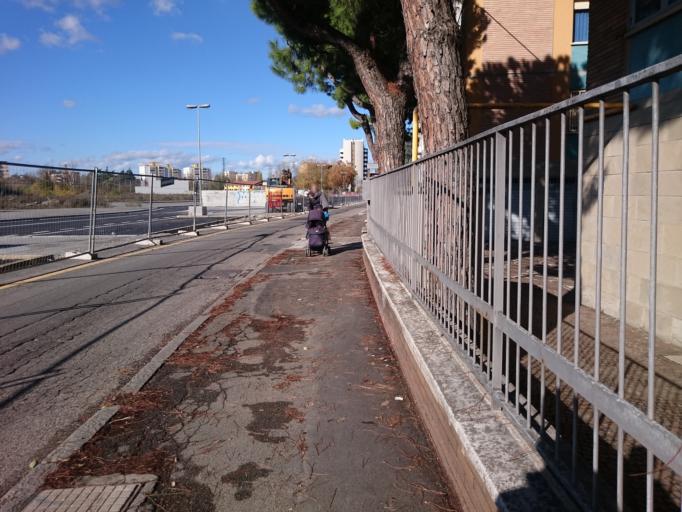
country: IT
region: Emilia-Romagna
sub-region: Provincia di Bologna
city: Bologna
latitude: 44.5147
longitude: 11.3380
